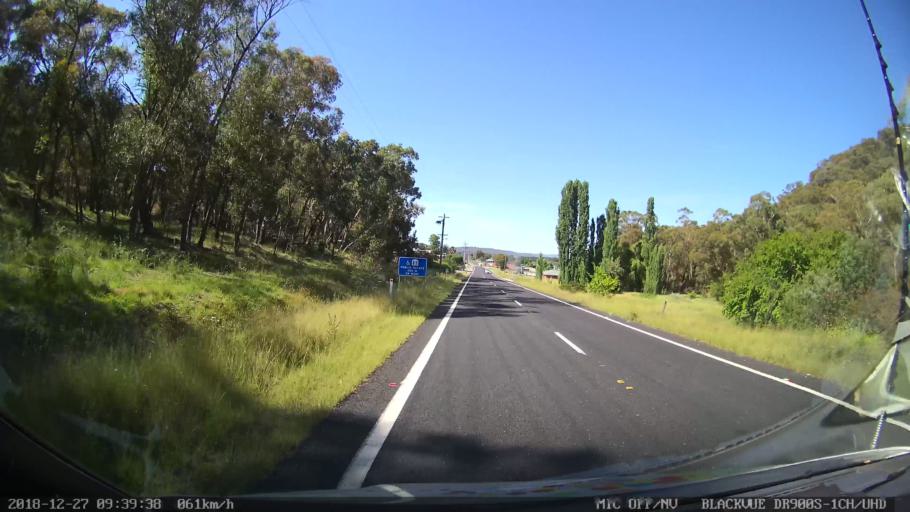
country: AU
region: New South Wales
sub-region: Lithgow
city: Portland
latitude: -33.2947
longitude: 150.0345
